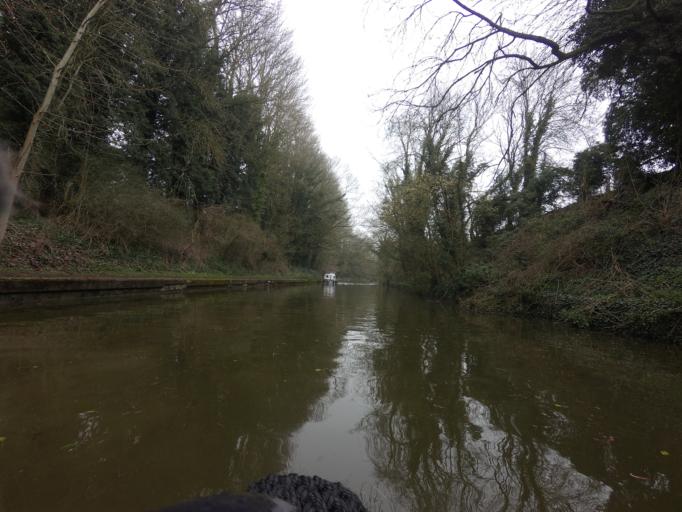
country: GB
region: England
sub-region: Hertfordshire
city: Tring
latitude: 51.7989
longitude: -0.6237
